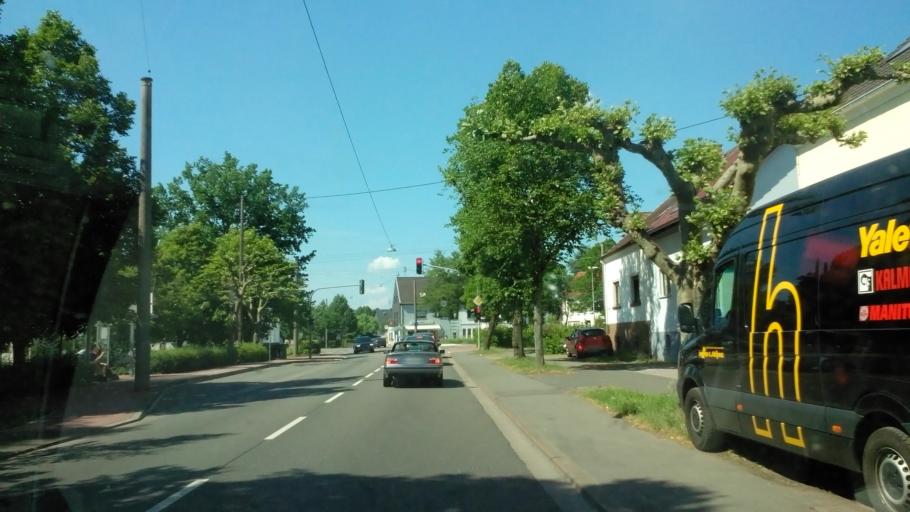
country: DE
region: Saarland
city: Saarwellingen
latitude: 49.3596
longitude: 6.8012
